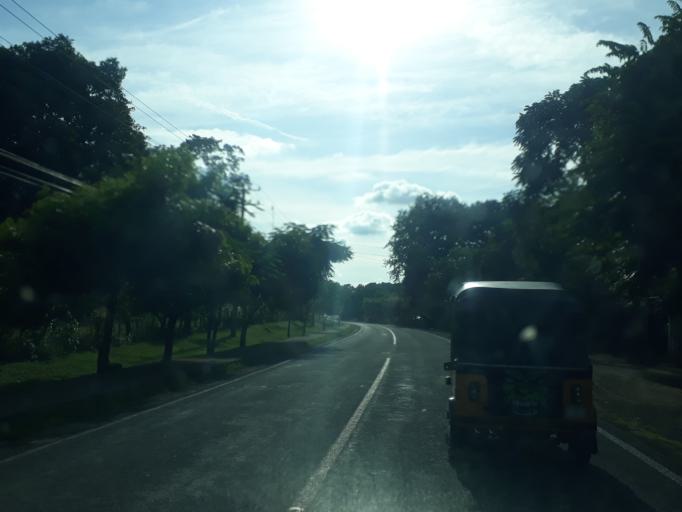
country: NI
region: Masaya
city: Masatepe
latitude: 11.9047
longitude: -86.1587
